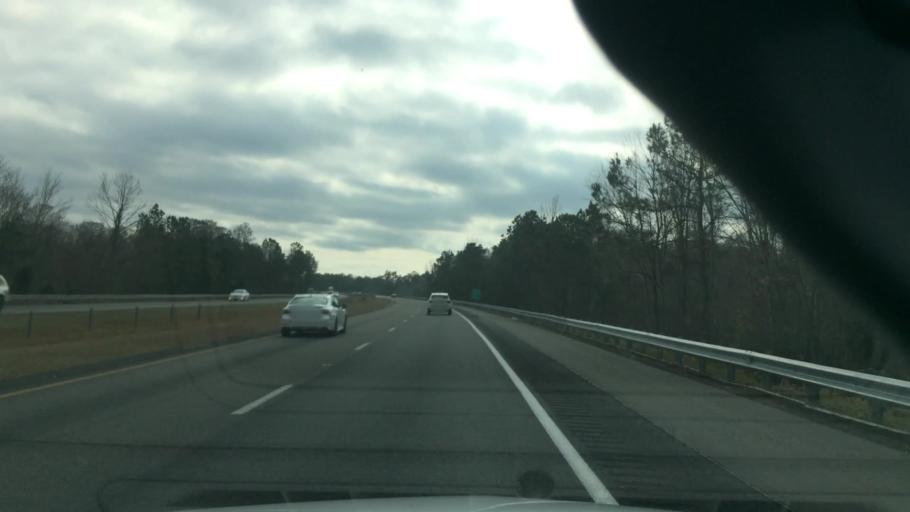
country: US
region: North Carolina
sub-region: New Hanover County
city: Castle Hayne
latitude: 34.3692
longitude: -77.8875
